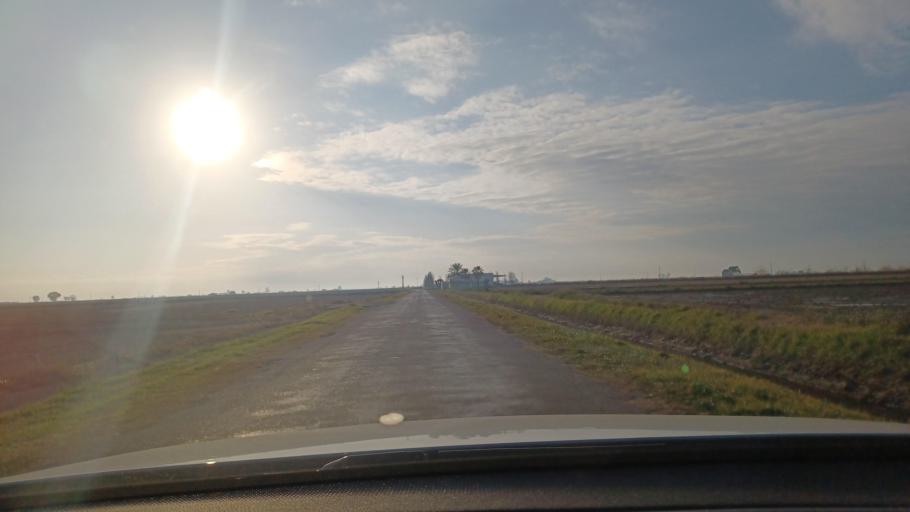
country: ES
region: Catalonia
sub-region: Provincia de Tarragona
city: Deltebre
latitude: 40.6857
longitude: 0.6542
